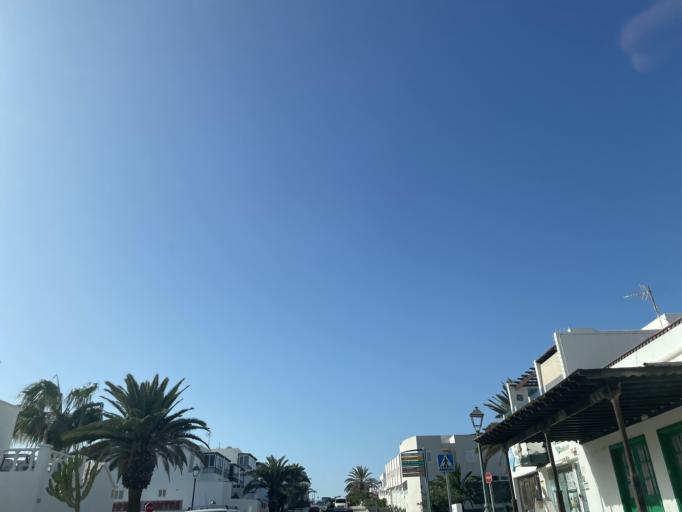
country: ES
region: Canary Islands
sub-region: Provincia de Las Palmas
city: Arrecife
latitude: 28.9962
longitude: -13.4966
